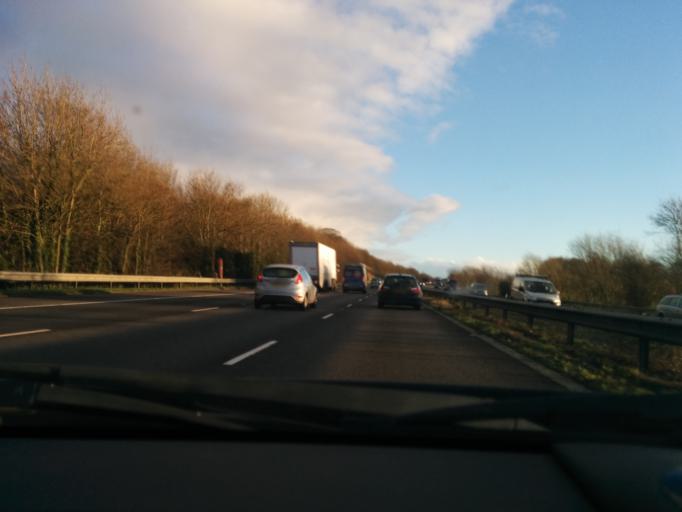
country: GB
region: England
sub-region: Oxfordshire
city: Thame
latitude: 51.7022
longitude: -0.9958
